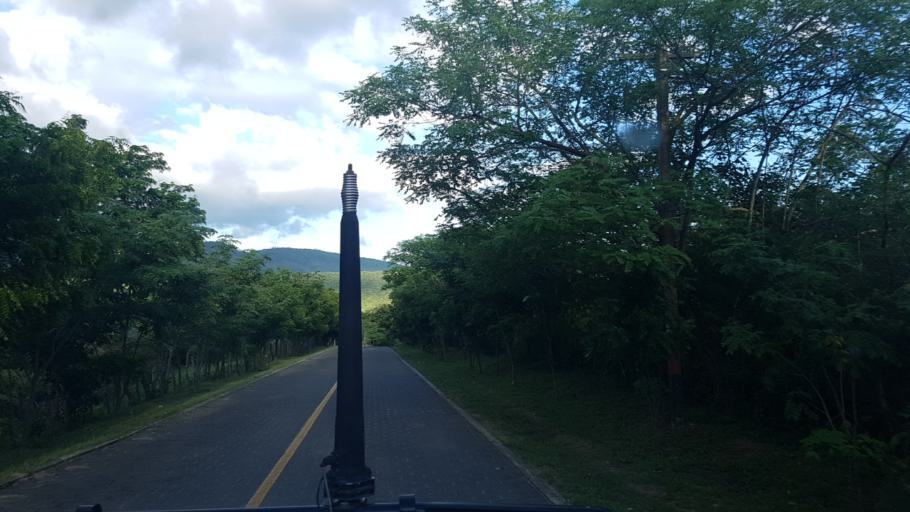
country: NI
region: Nueva Segovia
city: Ocotal
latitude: 13.6433
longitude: -86.6009
